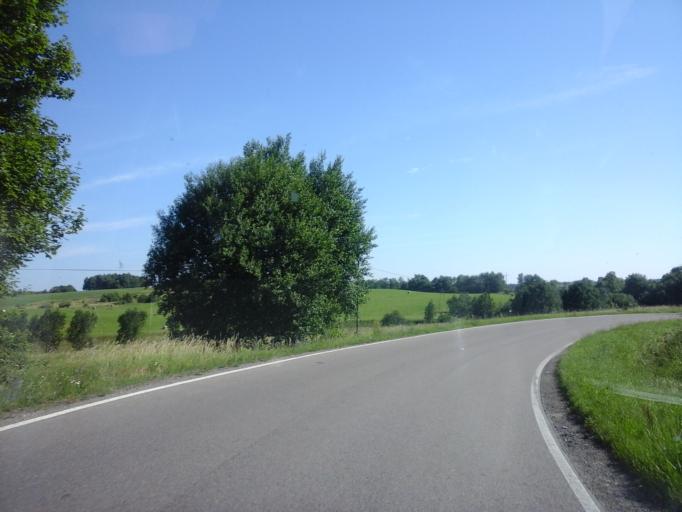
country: PL
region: West Pomeranian Voivodeship
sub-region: Powiat drawski
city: Zlocieniec
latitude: 53.6257
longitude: 15.9223
